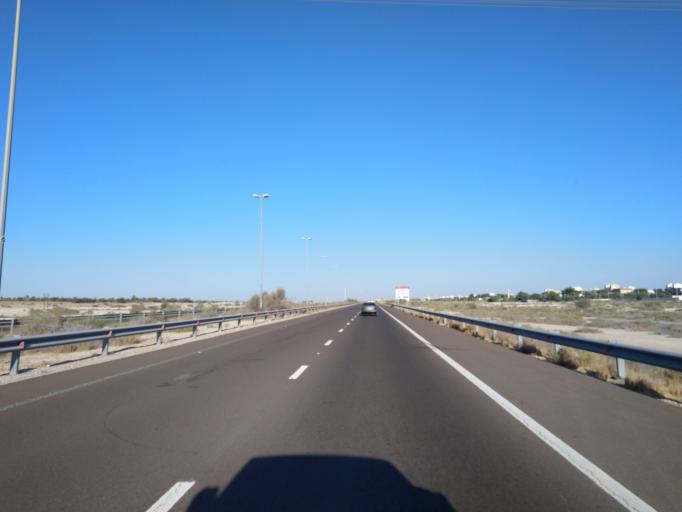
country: OM
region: Al Buraimi
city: Al Buraymi
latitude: 24.5204
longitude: 55.5229
